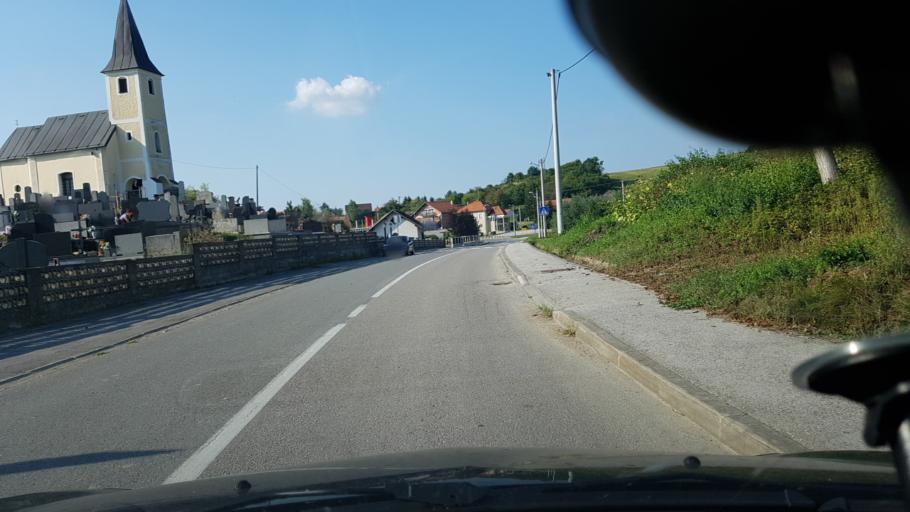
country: HR
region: Zagrebacka
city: Pojatno
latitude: 45.9508
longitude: 15.7325
